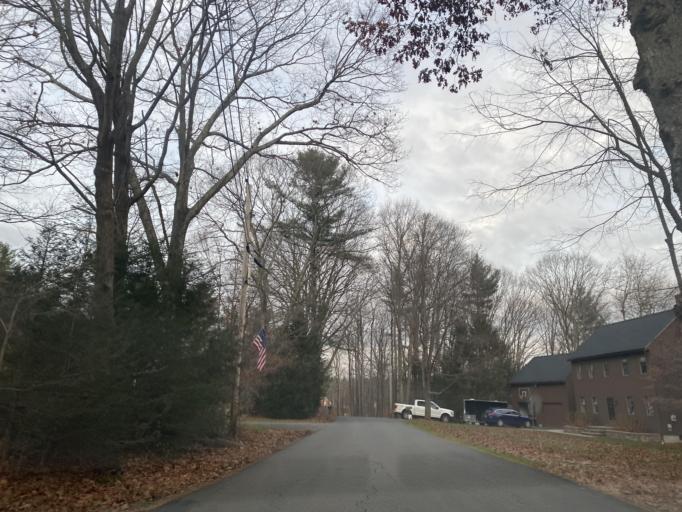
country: US
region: Massachusetts
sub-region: Worcester County
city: Spencer
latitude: 42.2601
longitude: -71.9541
